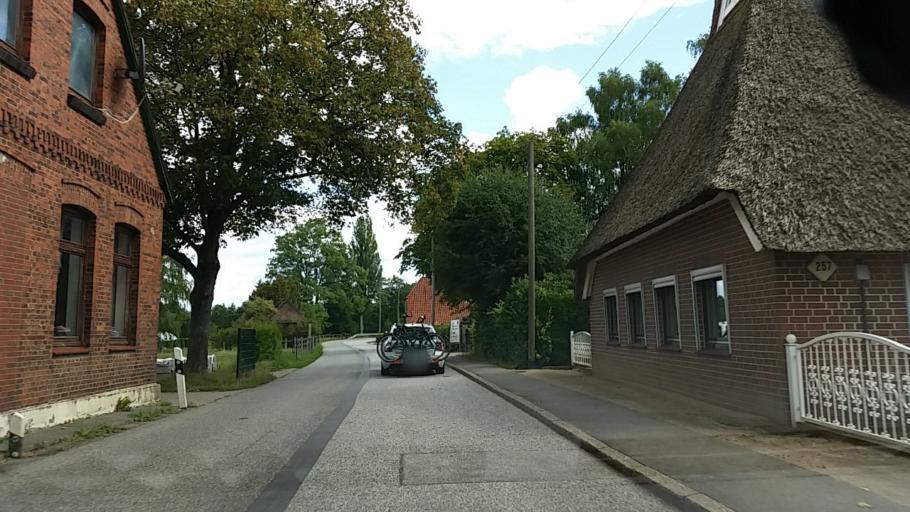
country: DE
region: Schleswig-Holstein
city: Bornsen
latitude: 53.4618
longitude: 10.2728
